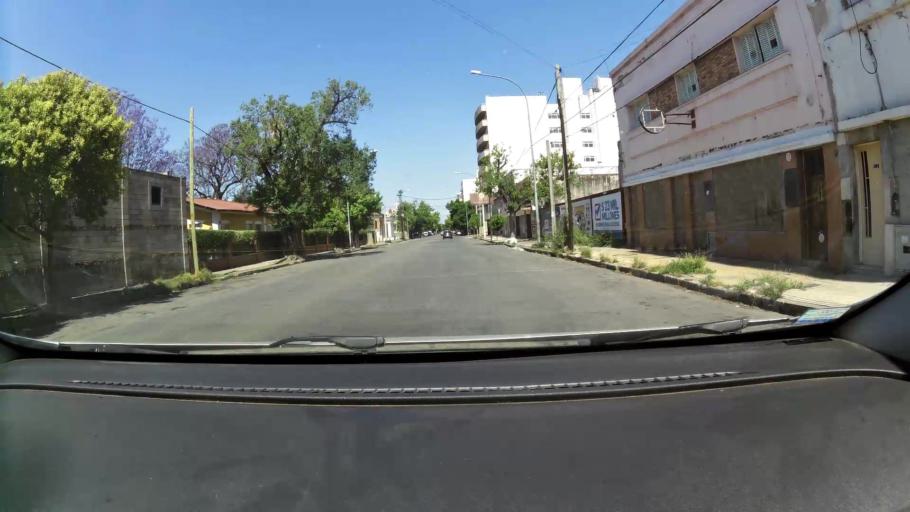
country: AR
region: Cordoba
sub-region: Departamento de Capital
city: Cordoba
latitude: -31.3991
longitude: -64.1792
